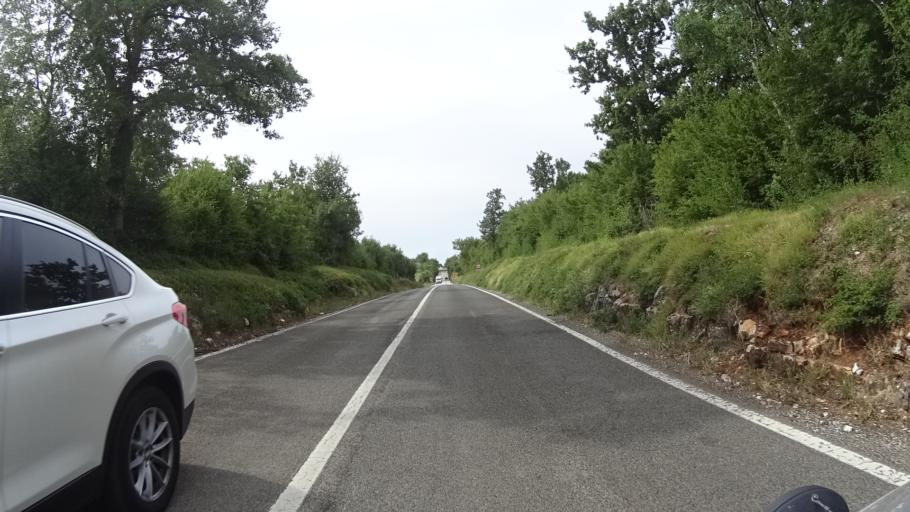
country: HR
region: Istarska
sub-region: Grad Rovinj
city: Rovinj
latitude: 45.1158
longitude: 13.7671
